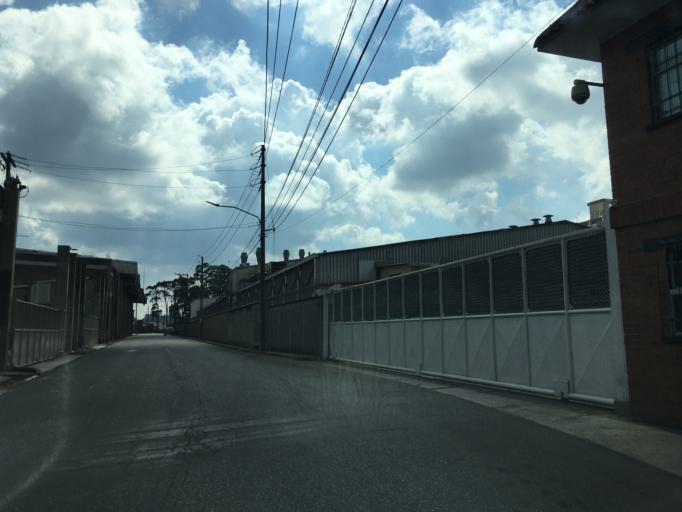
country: GT
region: Guatemala
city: Santa Catarina Pinula
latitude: 14.5573
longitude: -90.4540
